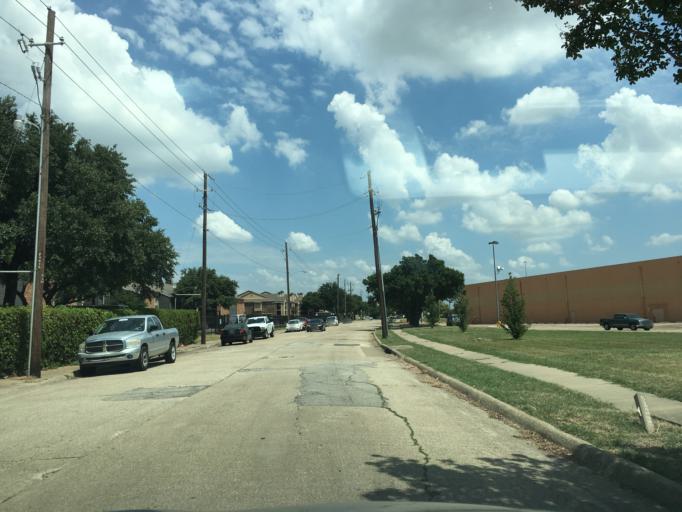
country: US
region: Texas
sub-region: Dallas County
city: Garland
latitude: 32.8674
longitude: -96.6787
